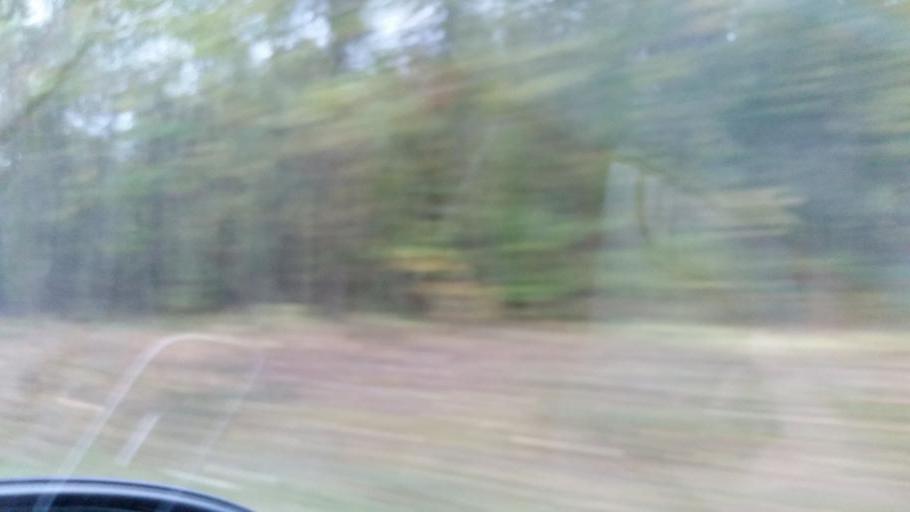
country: LU
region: Grevenmacher
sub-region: Canton de Grevenmacher
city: Mertert
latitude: 49.6828
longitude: 6.4815
